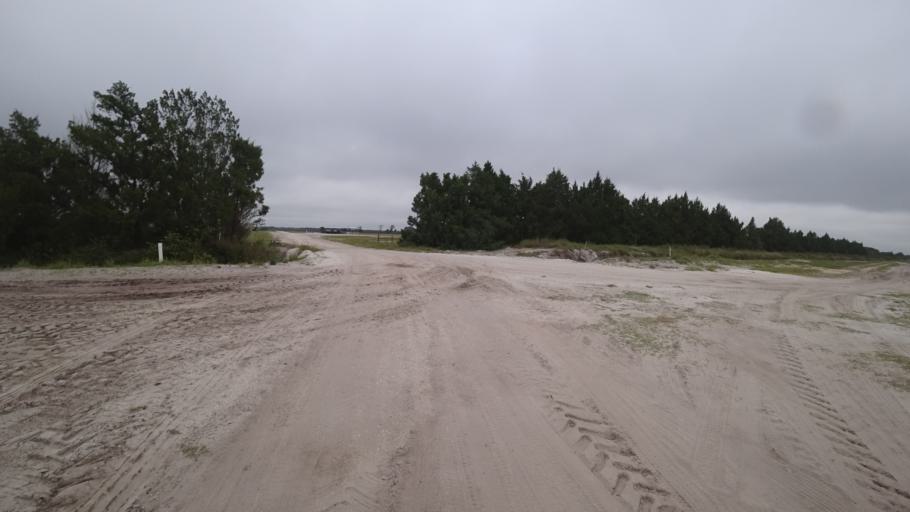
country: US
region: Florida
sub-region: Sarasota County
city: Warm Mineral Springs
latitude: 27.3012
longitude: -82.1471
